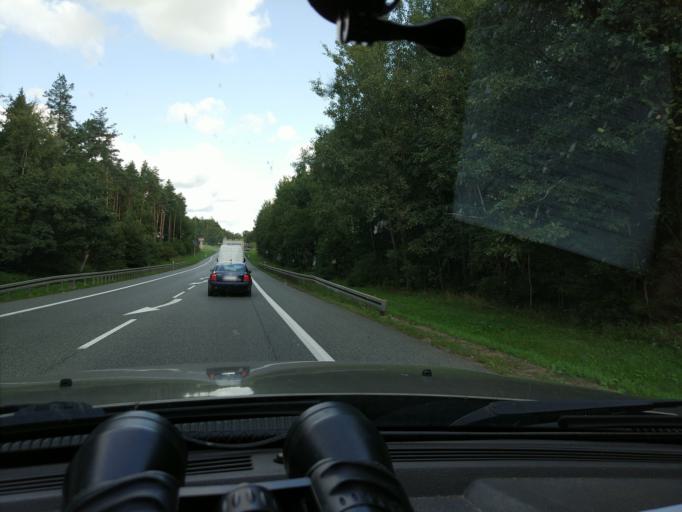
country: PL
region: Masovian Voivodeship
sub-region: Powiat mlawski
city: Mlawa
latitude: 53.1425
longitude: 20.3994
